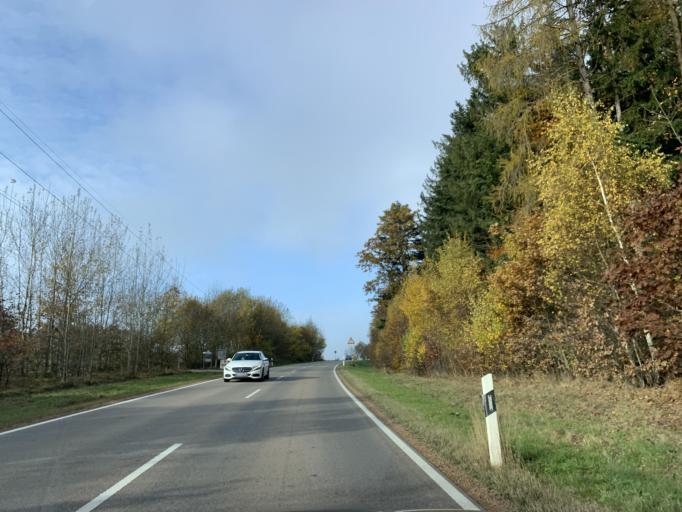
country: DE
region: Bavaria
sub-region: Upper Palatinate
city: Brunn
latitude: 49.2401
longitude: 12.2214
